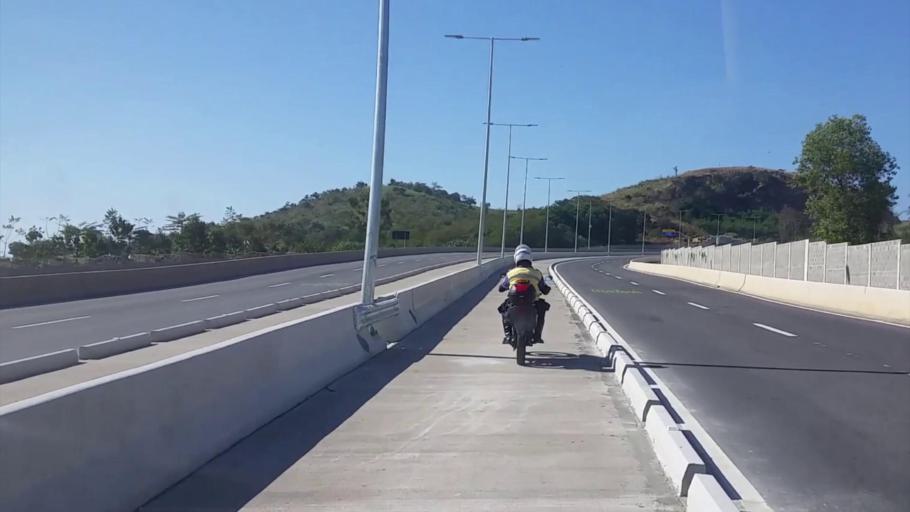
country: BR
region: Rio de Janeiro
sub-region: Nilopolis
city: Nilopolis
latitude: -22.8708
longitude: -43.4102
